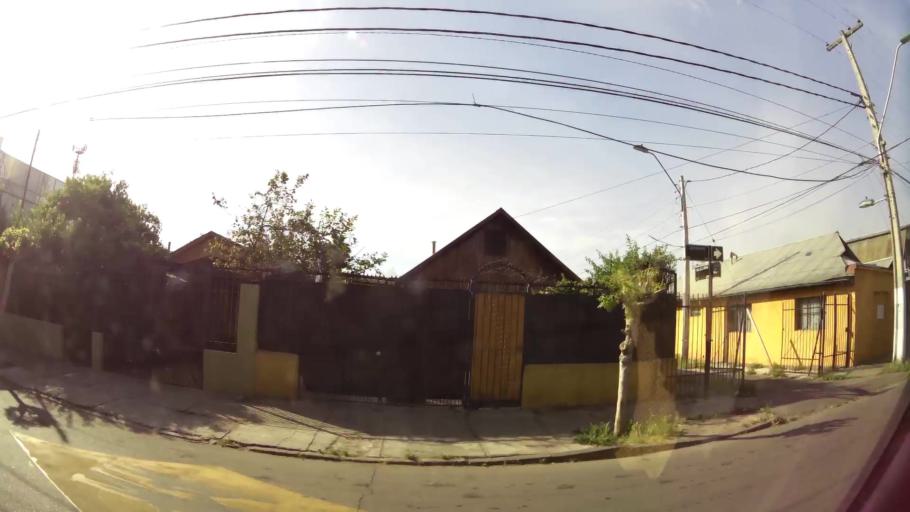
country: CL
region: Santiago Metropolitan
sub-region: Provincia de Santiago
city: La Pintana
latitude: -33.5239
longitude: -70.6356
